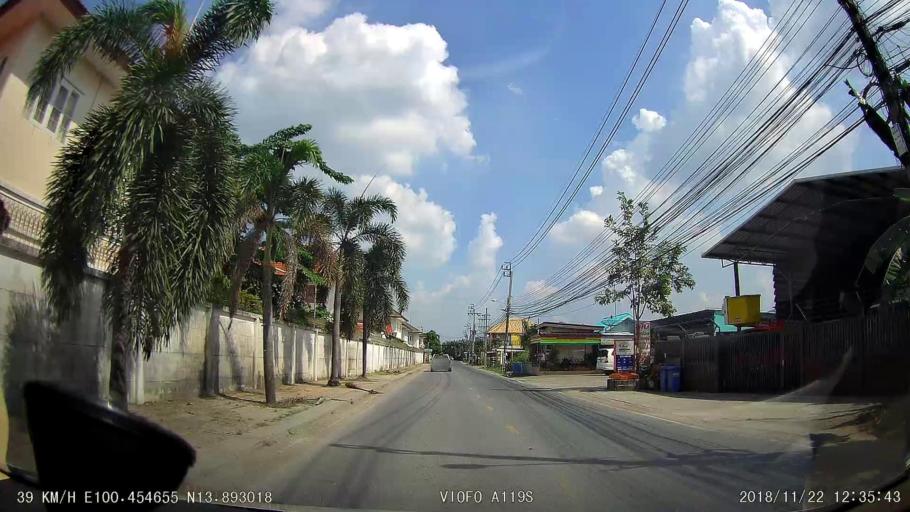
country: TH
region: Nonthaburi
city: Bang Bua Thong
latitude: 13.8930
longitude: 100.4549
